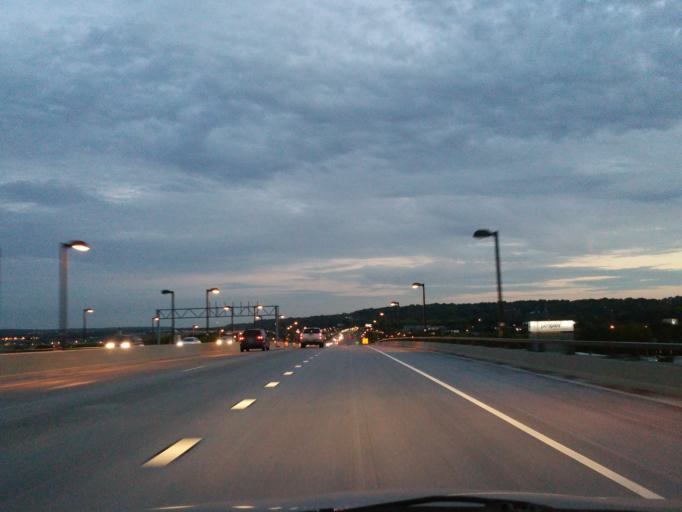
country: US
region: Minnesota
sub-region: Ramsey County
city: Saint Paul
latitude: 44.9468
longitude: -93.0794
